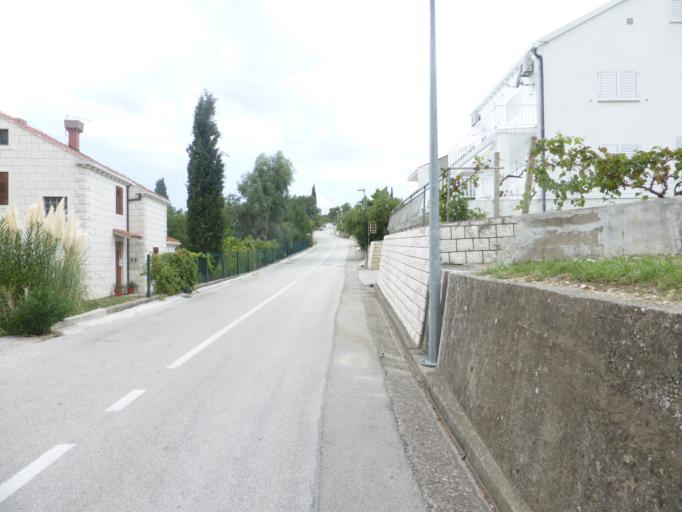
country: HR
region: Dubrovacko-Neretvanska
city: Podgora
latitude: 42.7836
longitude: 17.8756
